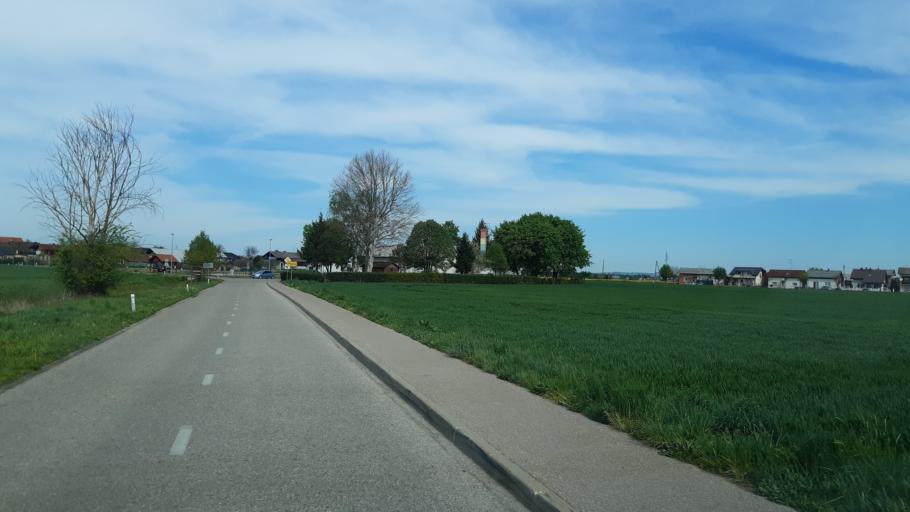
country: SI
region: Murska Sobota
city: Krog
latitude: 46.6527
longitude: 16.1423
